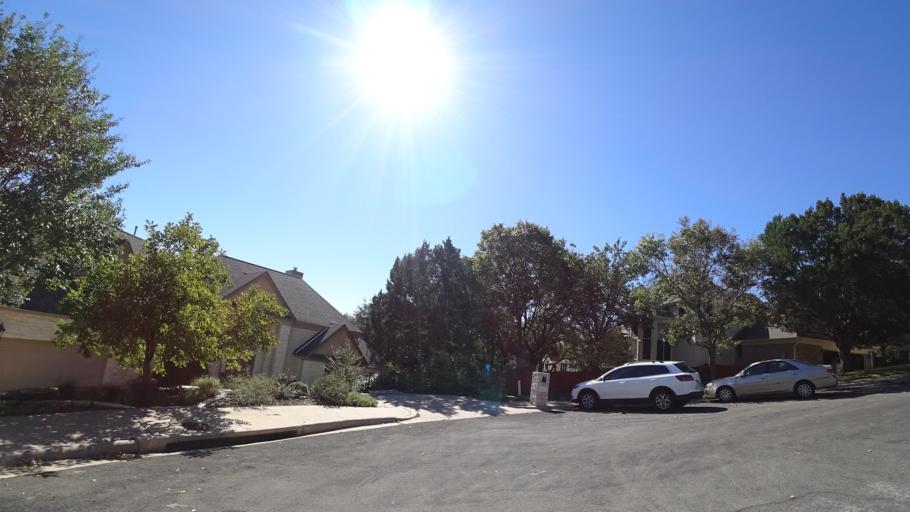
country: US
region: Texas
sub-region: Travis County
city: West Lake Hills
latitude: 30.3457
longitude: -97.7748
